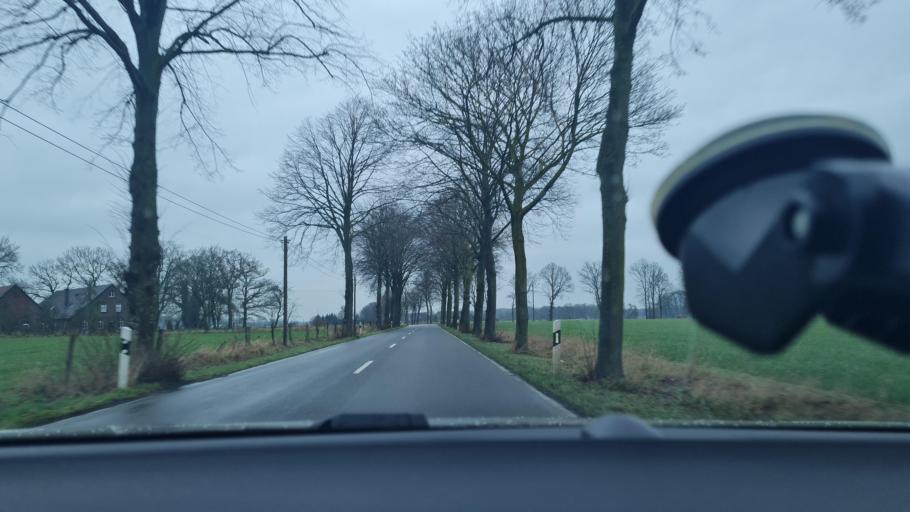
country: DE
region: North Rhine-Westphalia
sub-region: Regierungsbezirk Dusseldorf
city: Hunxe
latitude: 51.7039
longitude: 6.7463
